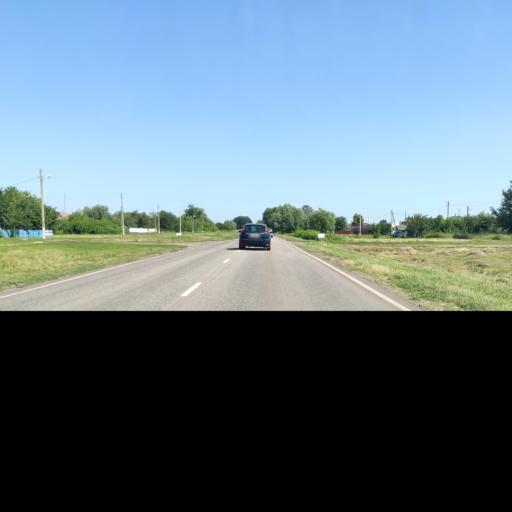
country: RU
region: Voronezj
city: Verkhnyaya Khava
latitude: 51.6709
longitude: 39.9557
